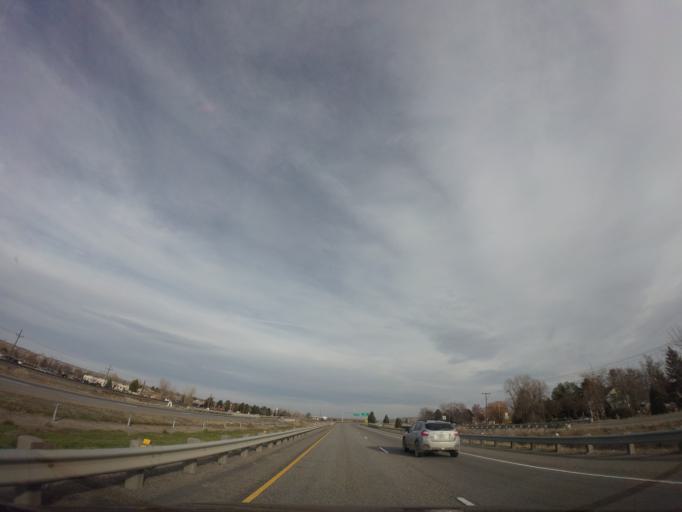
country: US
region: Montana
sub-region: Yellowstone County
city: Billings
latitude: 45.7489
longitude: -108.5693
